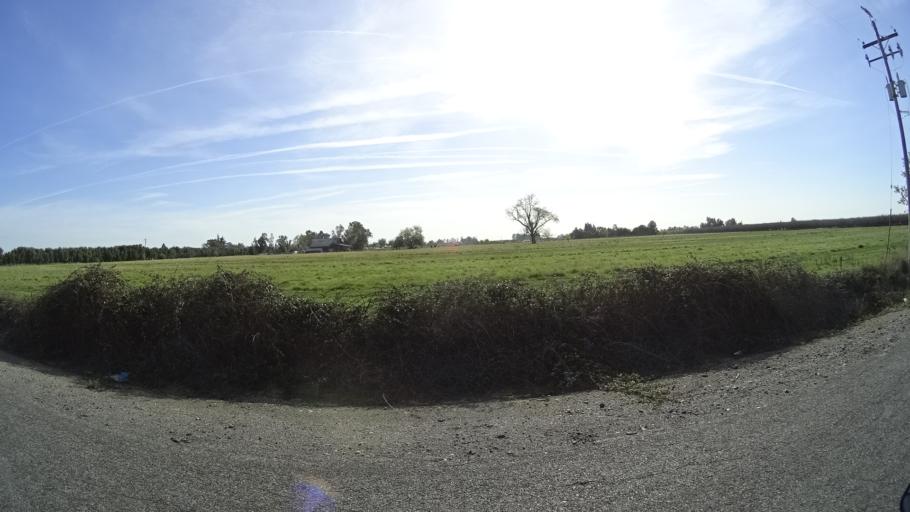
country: US
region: California
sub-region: Glenn County
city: Orland
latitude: 39.7099
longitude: -122.2162
